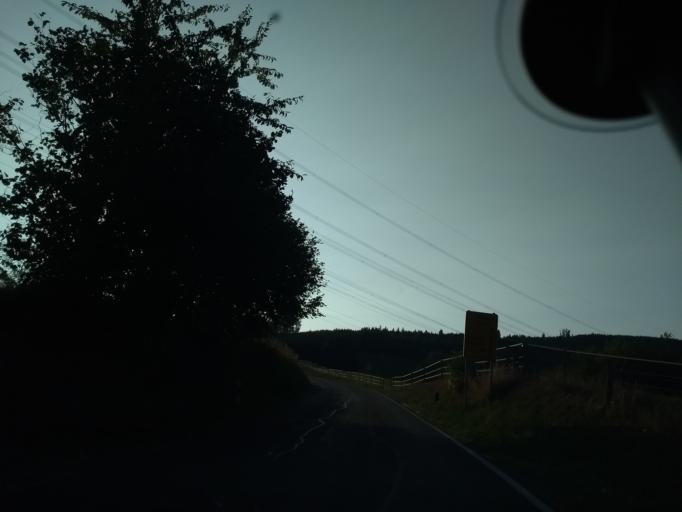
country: DE
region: North Rhine-Westphalia
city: Eslohe
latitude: 51.2800
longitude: 8.0830
